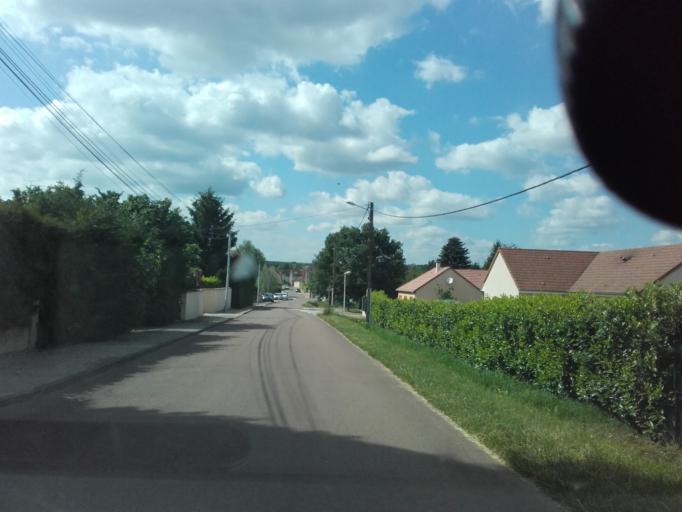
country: FR
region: Bourgogne
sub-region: Departement de Saone-et-Loire
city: Chagny
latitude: 46.8969
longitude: 4.7713
